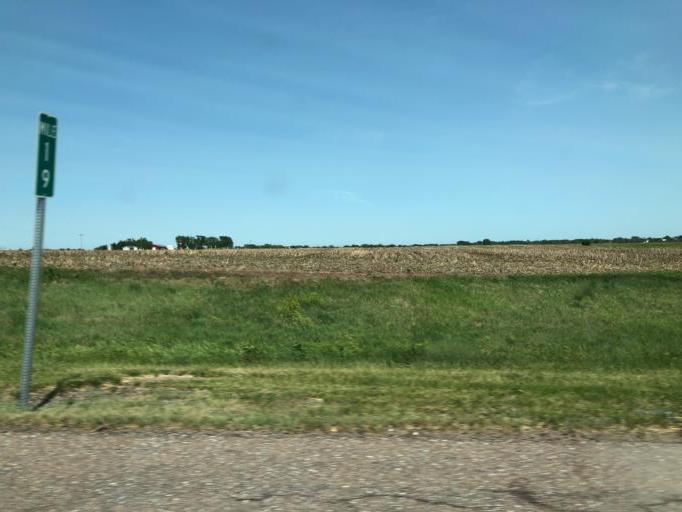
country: US
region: Nebraska
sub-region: Thayer County
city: Hebron
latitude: 40.2615
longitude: -97.5765
